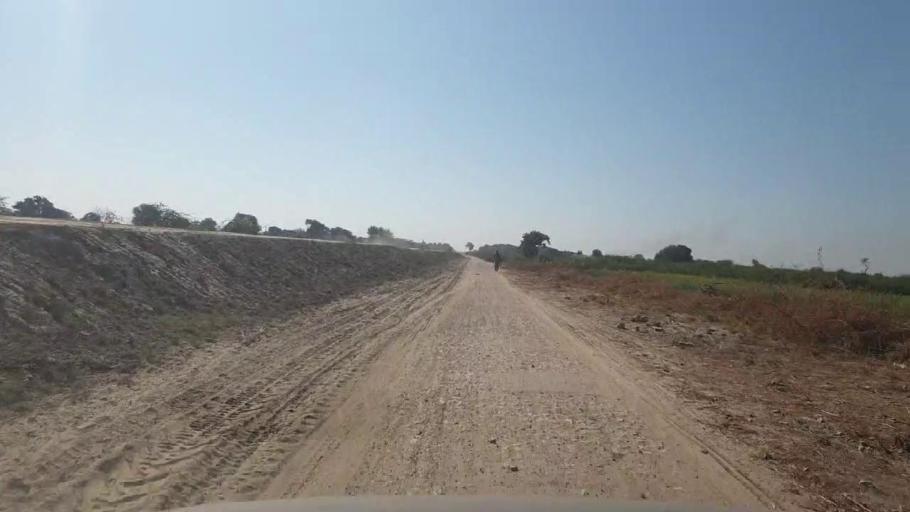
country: PK
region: Sindh
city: Mirwah Gorchani
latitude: 25.2882
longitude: 69.1033
